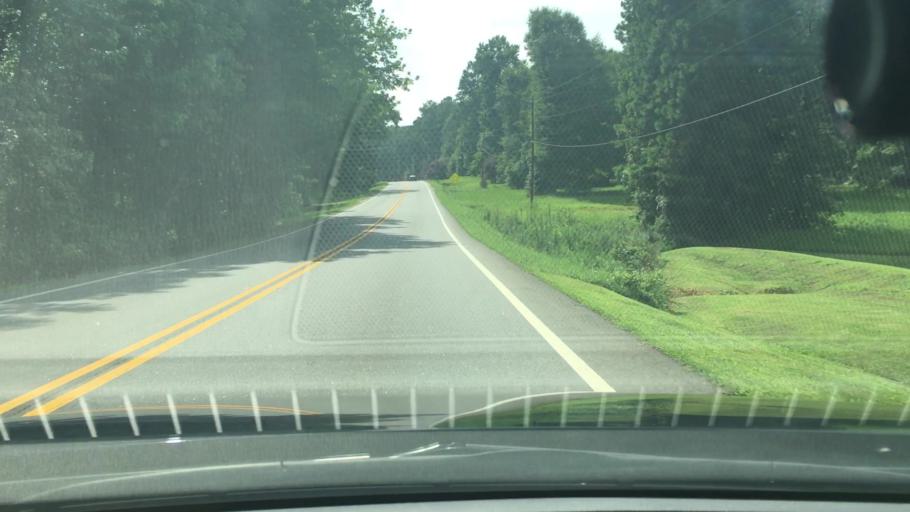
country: US
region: Georgia
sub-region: Coweta County
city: East Newnan
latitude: 33.3360
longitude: -84.7353
